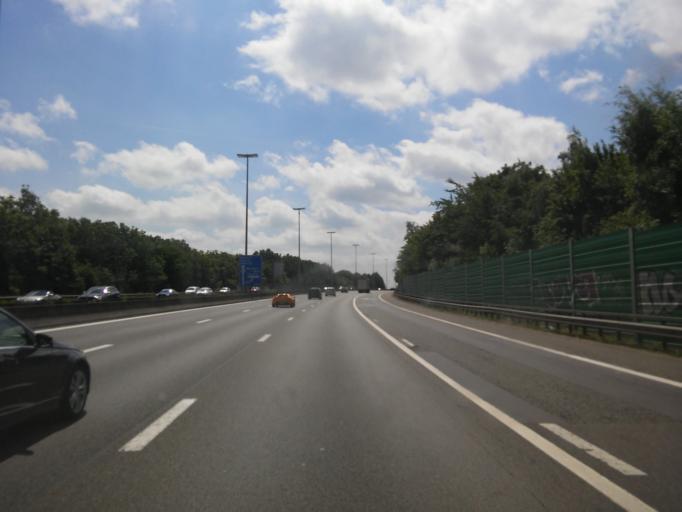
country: BE
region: Flanders
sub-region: Provincie Vlaams-Brabant
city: Kraainem
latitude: 50.8607
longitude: 4.4744
